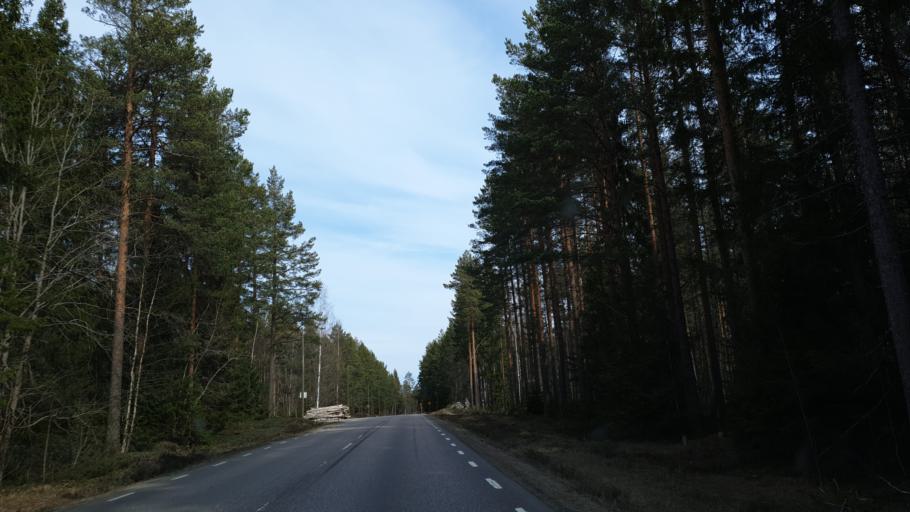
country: SE
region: Gaevleborg
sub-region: Gavle Kommun
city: Norrsundet
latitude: 60.9963
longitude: 17.0892
